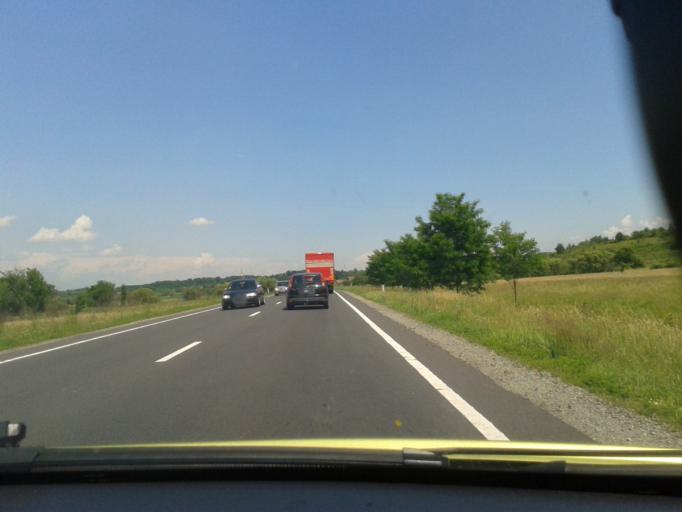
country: RO
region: Sibiu
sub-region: Comuna Carta
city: Carta
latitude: 45.7578
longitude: 24.5115
